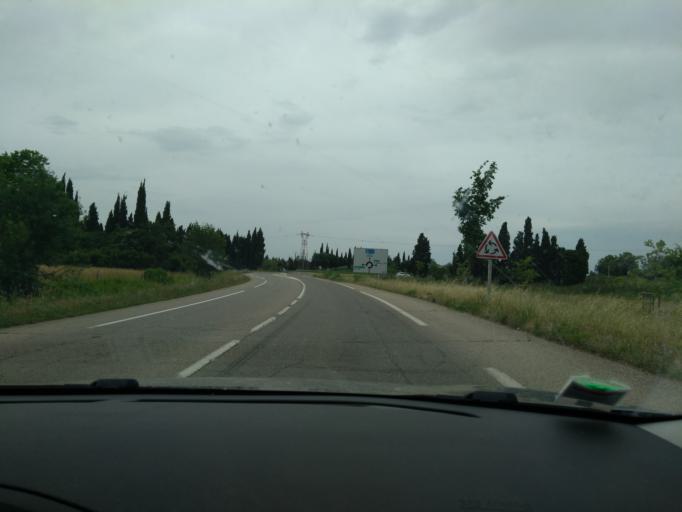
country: FR
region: Provence-Alpes-Cote d'Azur
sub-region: Departement des Bouches-du-Rhone
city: Eyguieres
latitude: 43.6430
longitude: 5.0208
